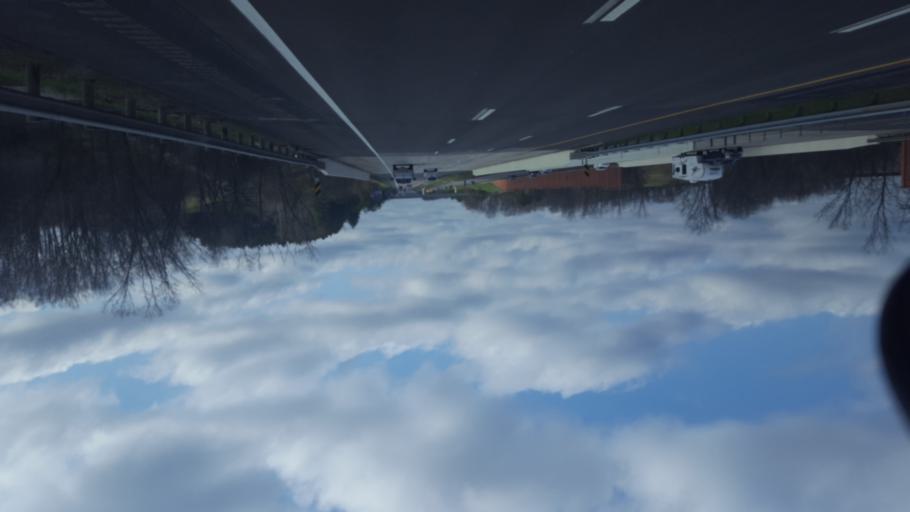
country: US
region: Ohio
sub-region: Medina County
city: Medina
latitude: 41.1120
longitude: -81.8120
